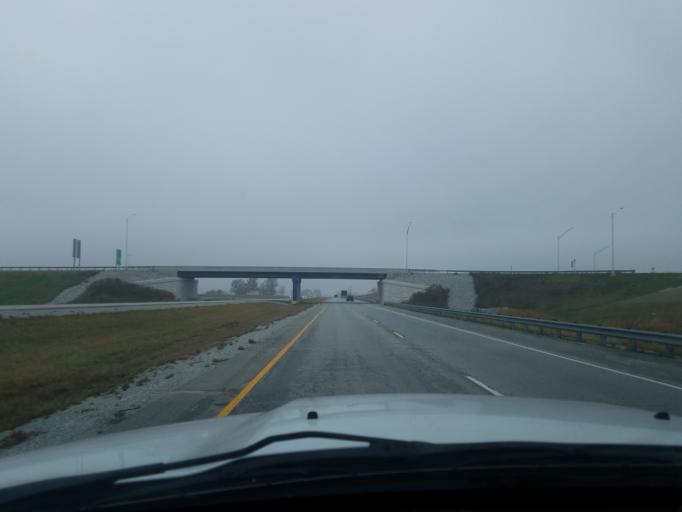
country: US
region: Indiana
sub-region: Tipton County
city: Tipton
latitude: 40.2739
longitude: -86.1270
